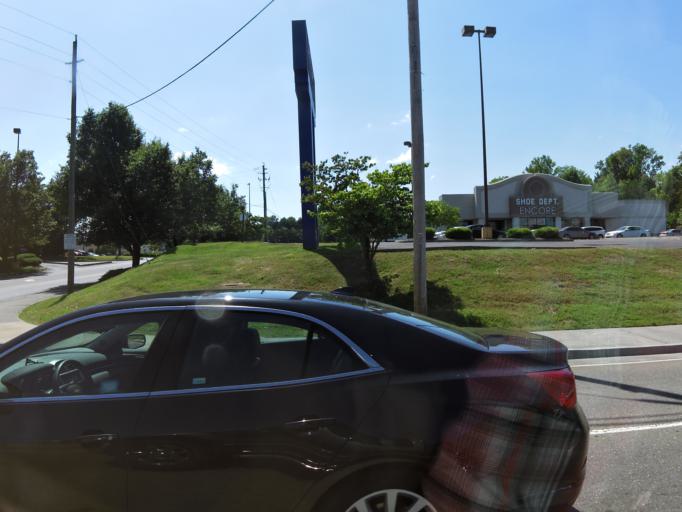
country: US
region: Tennessee
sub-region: Sevier County
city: Sevierville
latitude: 35.8401
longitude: -83.5711
